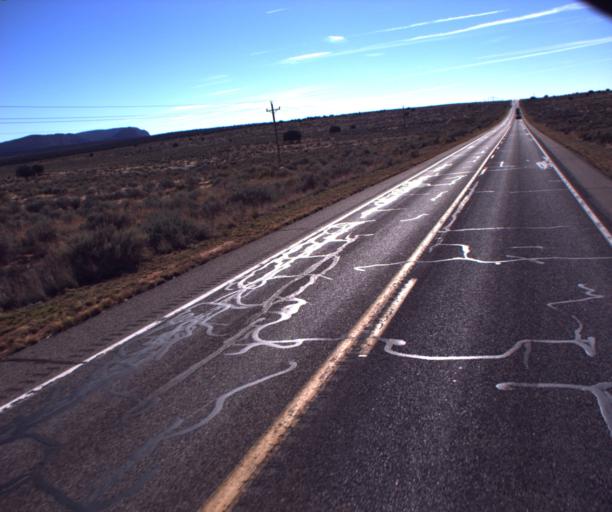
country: US
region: Arizona
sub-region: Mohave County
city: Colorado City
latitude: 36.9127
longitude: -112.9291
